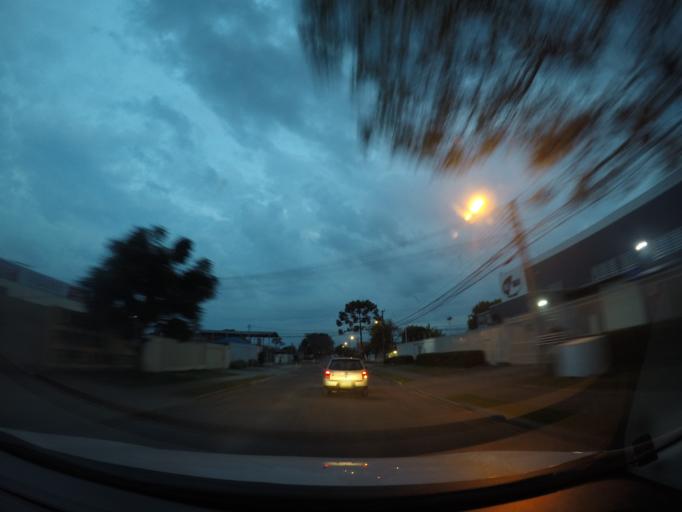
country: BR
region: Parana
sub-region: Sao Jose Dos Pinhais
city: Sao Jose dos Pinhais
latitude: -25.5136
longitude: -49.2262
